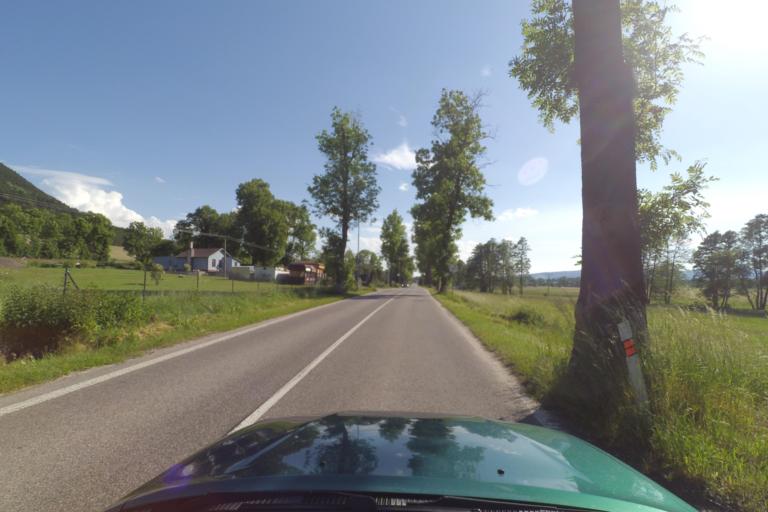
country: PL
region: Lower Silesian Voivodeship
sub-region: Powiat kamiennogorski
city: Lubawka
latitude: 50.6852
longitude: 15.9819
